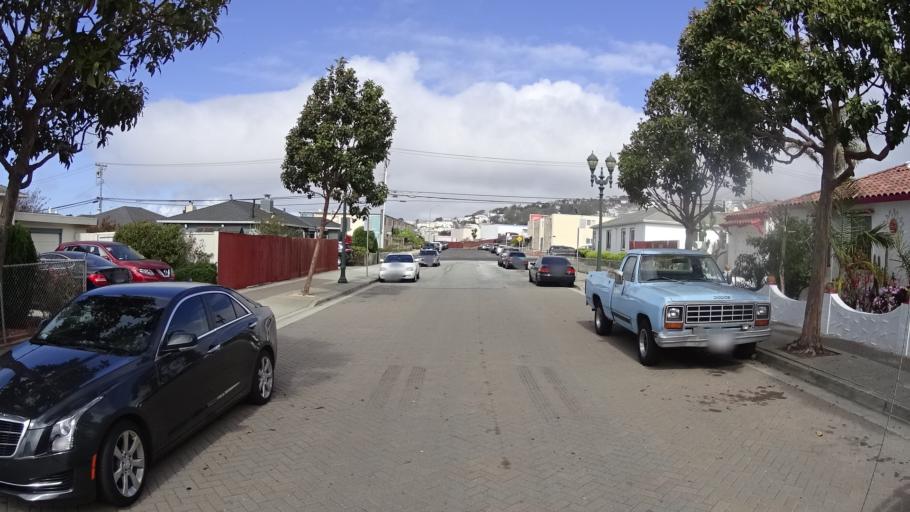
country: US
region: California
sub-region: San Mateo County
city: Colma
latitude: 37.6855
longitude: -122.4608
